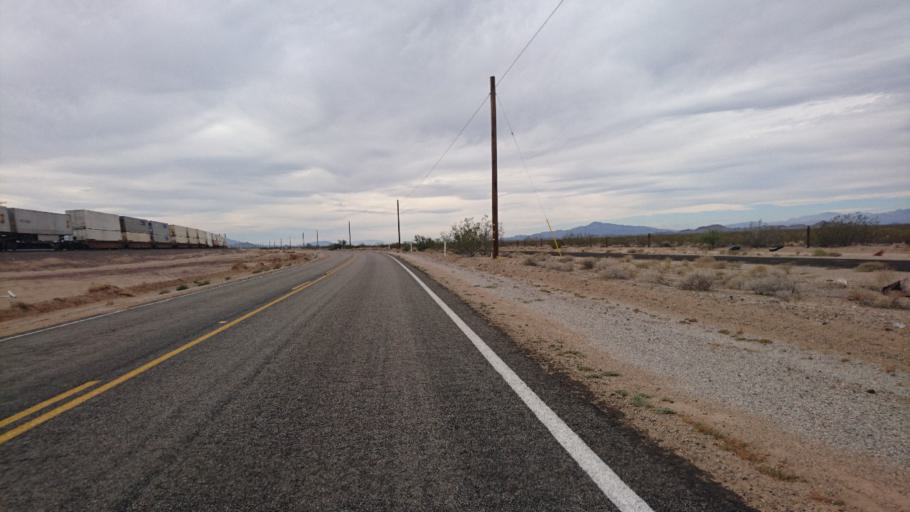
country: US
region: California
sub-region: San Bernardino County
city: Needles
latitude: 34.8986
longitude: -115.0924
